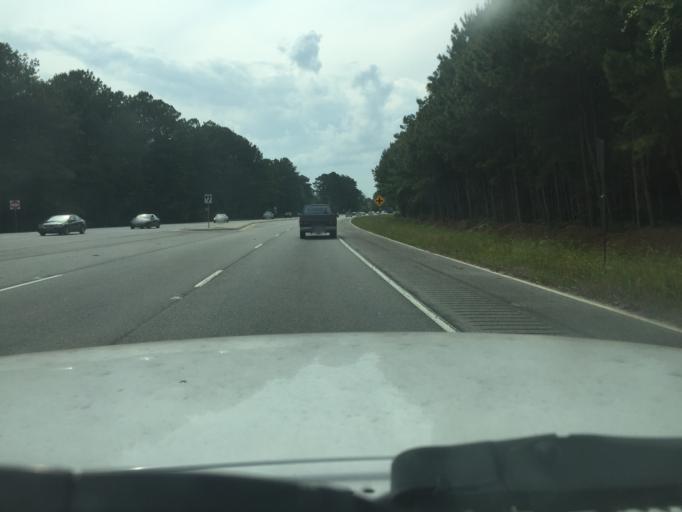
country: US
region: Georgia
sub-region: Chatham County
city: Wilmington Island
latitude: 32.0318
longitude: -80.9777
